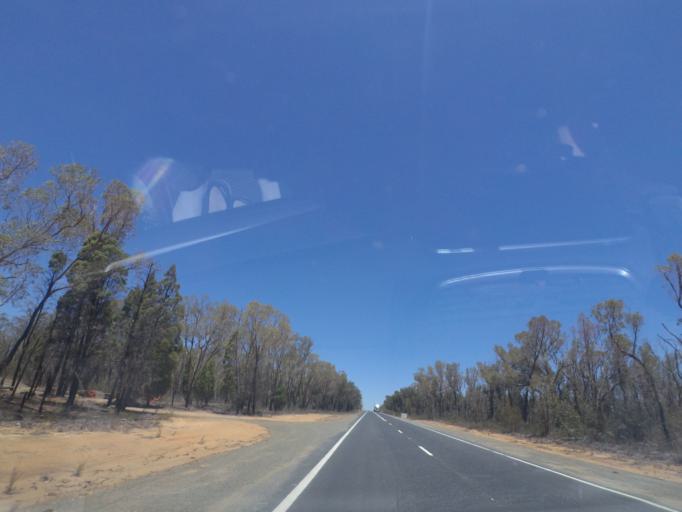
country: AU
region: New South Wales
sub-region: Warrumbungle Shire
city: Coonabarabran
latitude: -30.9599
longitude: 149.4198
